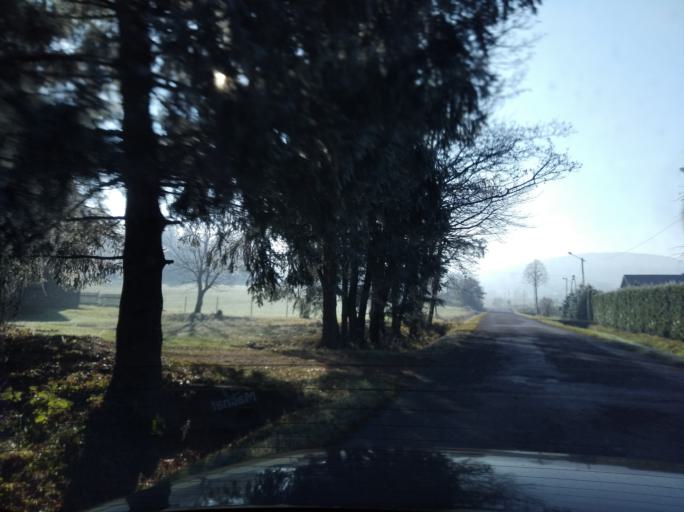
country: PL
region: Subcarpathian Voivodeship
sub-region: Powiat strzyzowski
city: Wysoka Strzyzowska
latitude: 49.8515
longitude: 21.7014
